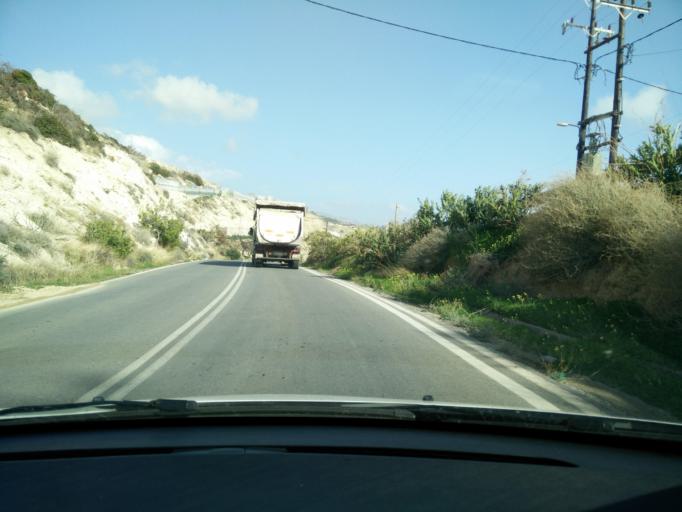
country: GR
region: Crete
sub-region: Nomos Lasithiou
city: Gra Liyia
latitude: 35.0080
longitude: 25.6238
